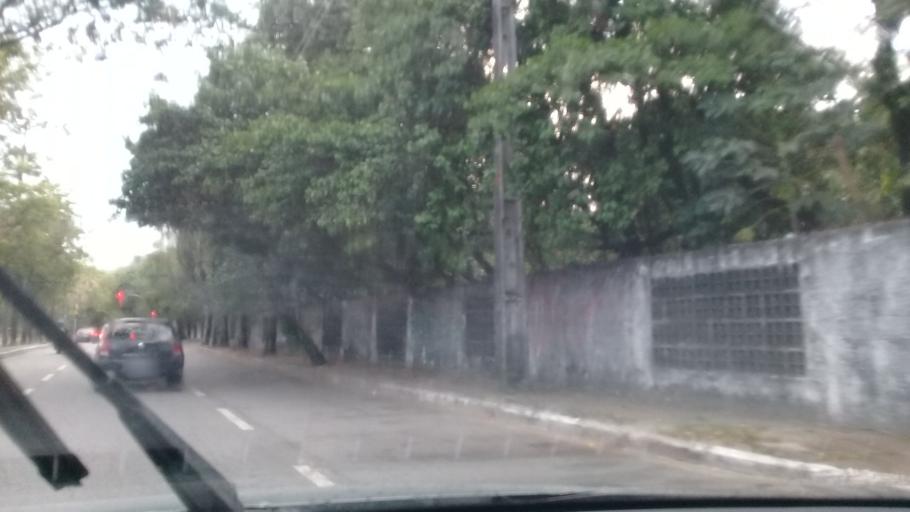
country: BR
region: Pernambuco
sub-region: Recife
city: Recife
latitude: -8.1179
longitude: -34.9065
